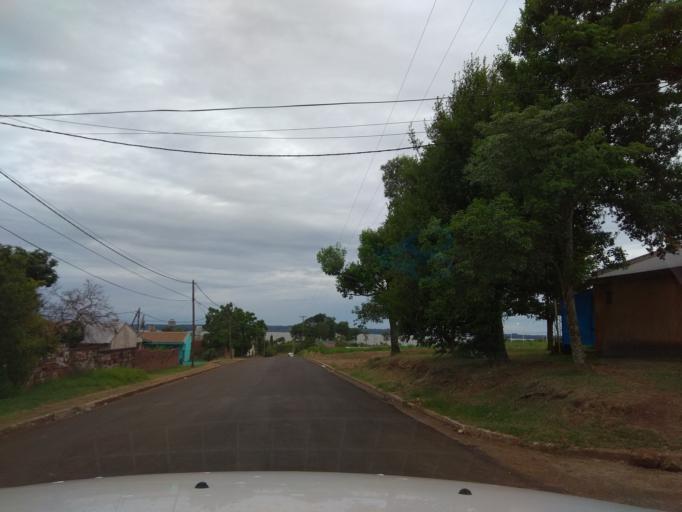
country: AR
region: Misiones
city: Garupa
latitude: -27.4476
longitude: -55.8536
